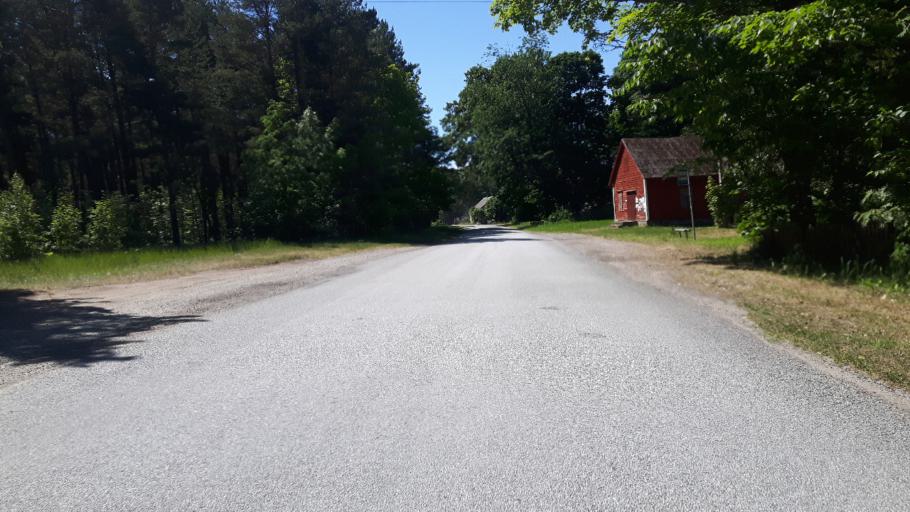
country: LV
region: Salacgrivas
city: Ainazi
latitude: 58.0366
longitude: 24.4631
